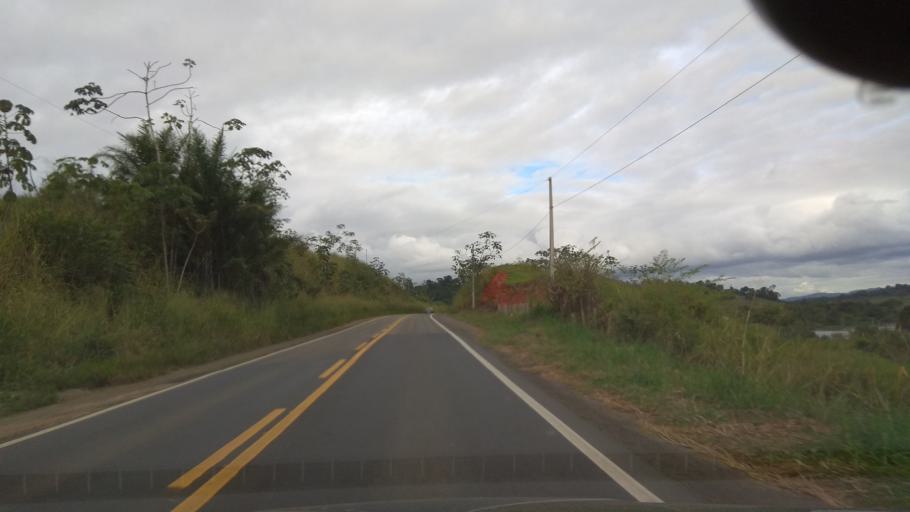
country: BR
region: Bahia
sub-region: Ipiau
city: Ipiau
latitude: -14.1781
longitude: -39.6686
